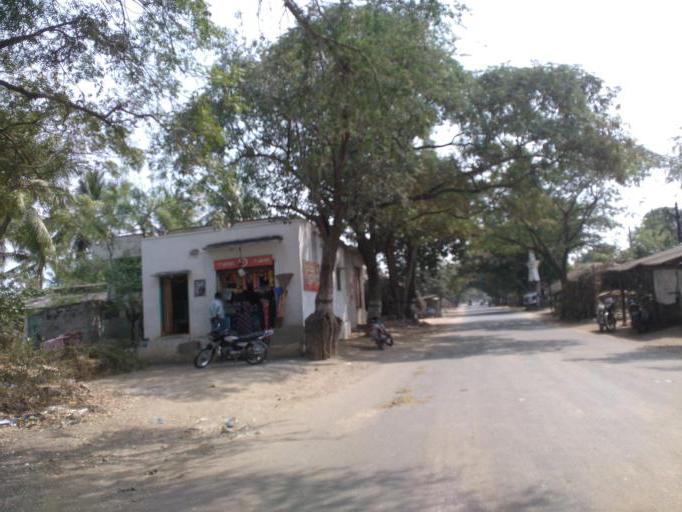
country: IN
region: Andhra Pradesh
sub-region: Prakasam
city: Chirala
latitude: 15.8254
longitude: 80.3780
